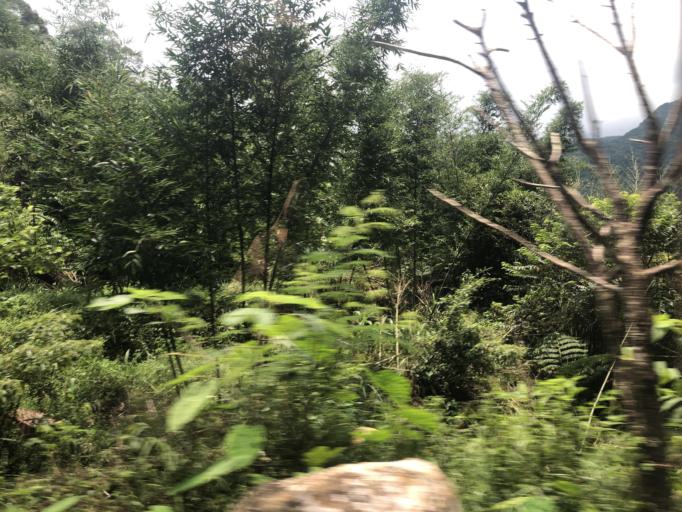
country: TW
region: Taiwan
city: Daxi
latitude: 24.8722
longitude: 121.4106
